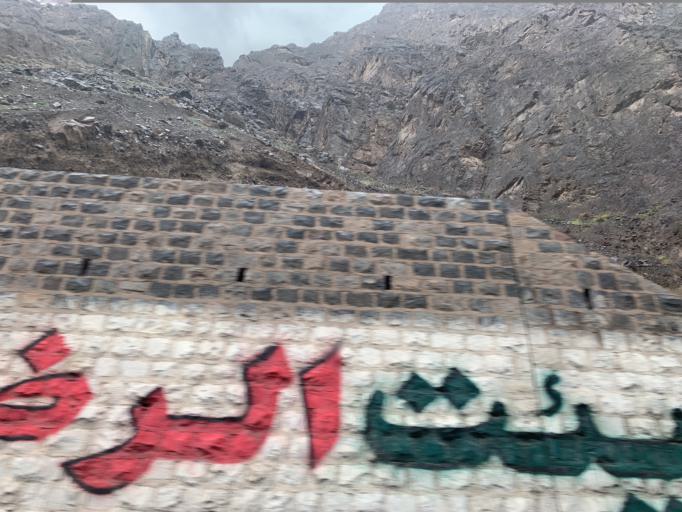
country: IR
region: Mazandaran
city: Amol
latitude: 36.1142
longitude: 52.2821
